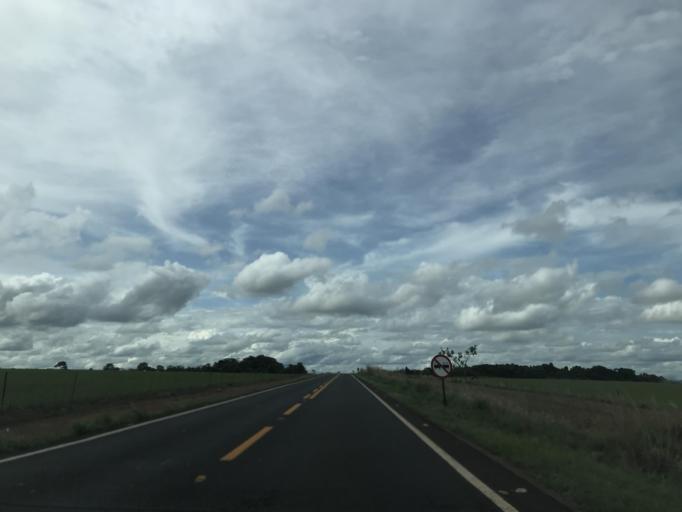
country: BR
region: Goias
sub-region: Piracanjuba
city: Piracanjuba
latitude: -17.4466
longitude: -48.7796
